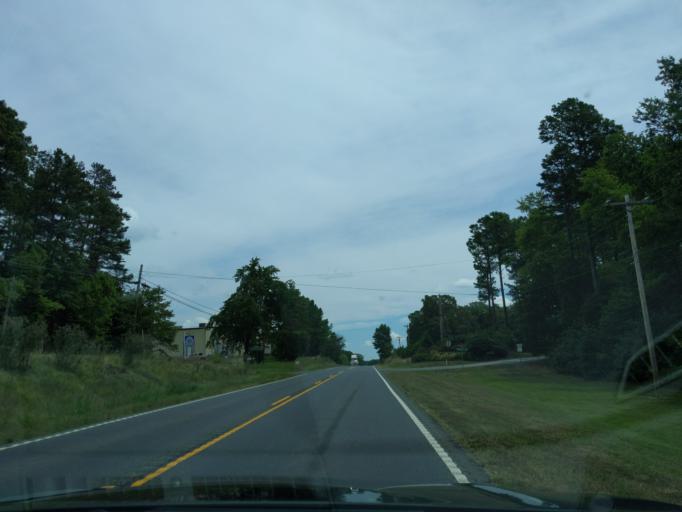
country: US
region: North Carolina
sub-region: Rowan County
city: Rockwell
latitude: 35.4624
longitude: -80.3067
